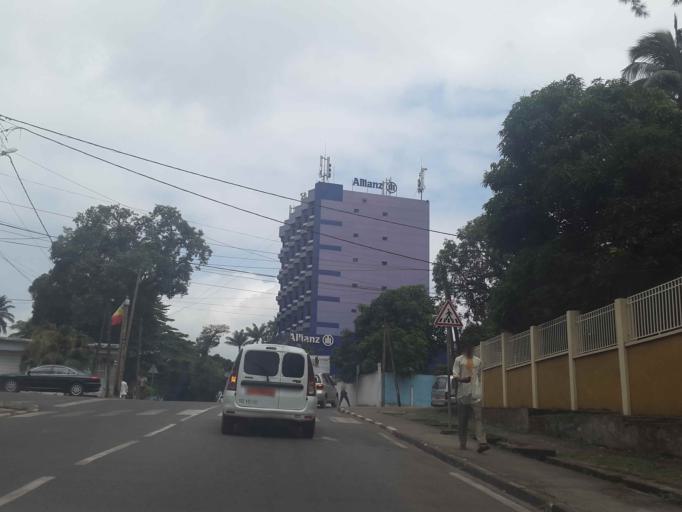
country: CM
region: Littoral
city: Douala
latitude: 4.0371
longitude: 9.6889
